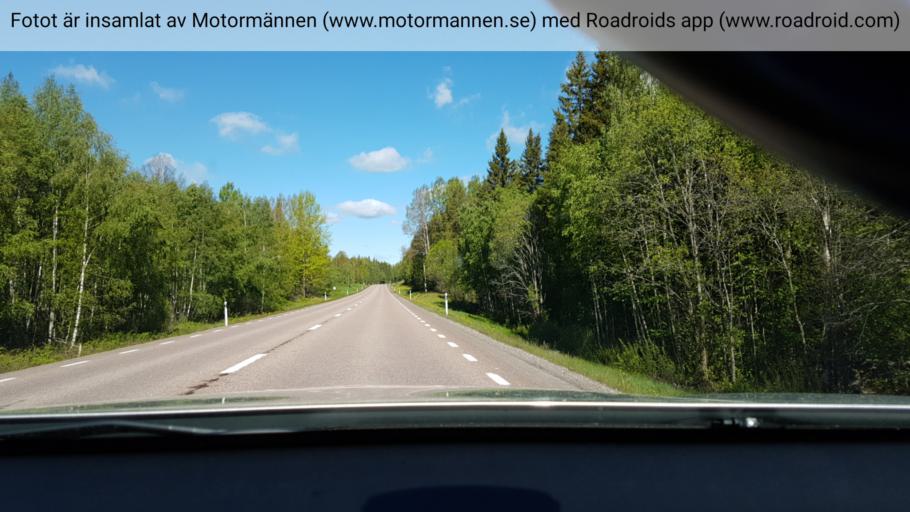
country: SE
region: Dalarna
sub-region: Faluns Kommun
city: Falun
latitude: 60.6482
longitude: 15.5661
